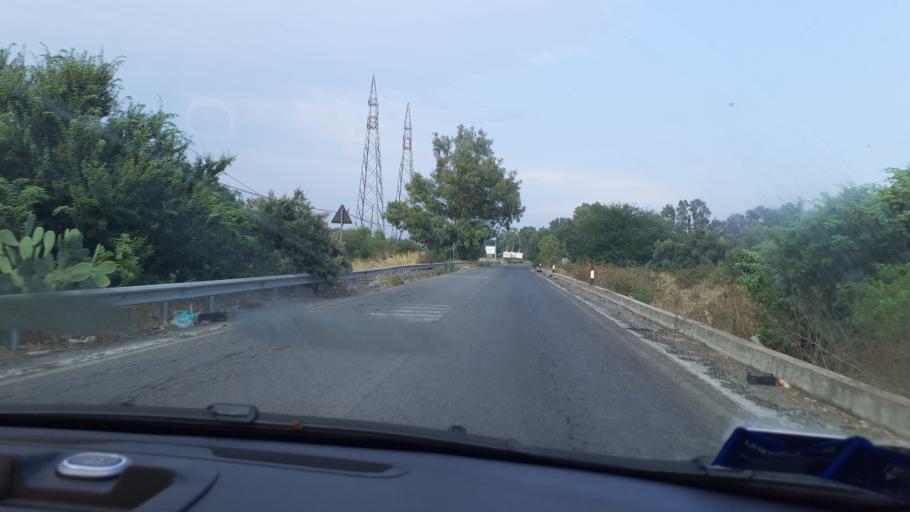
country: IT
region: Sicily
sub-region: Catania
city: Catania
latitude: 37.4486
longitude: 15.0206
